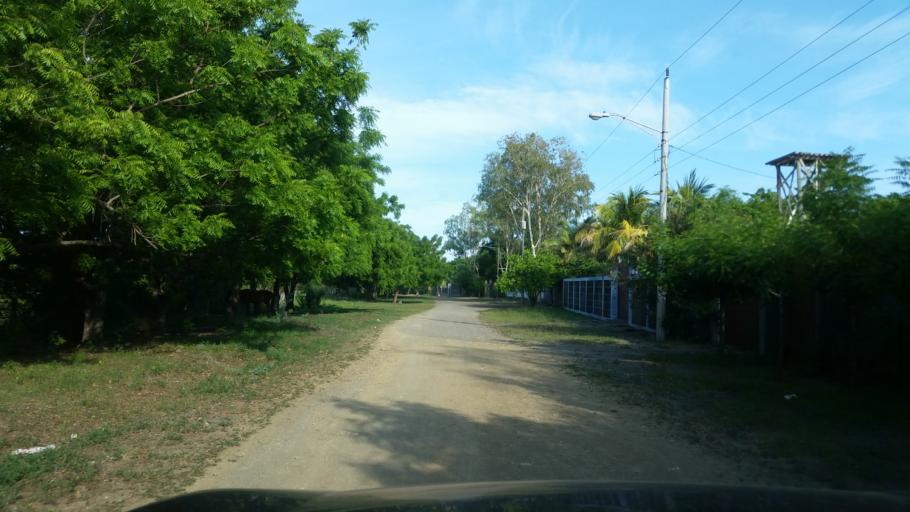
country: NI
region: Managua
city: Masachapa
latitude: 11.7541
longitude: -86.4854
